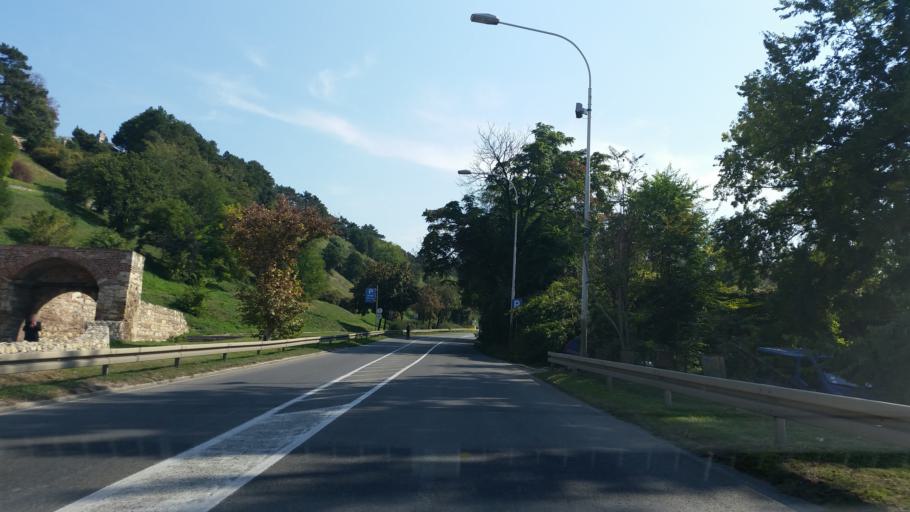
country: RS
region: Central Serbia
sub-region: Belgrade
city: Stari Grad
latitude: 44.8217
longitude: 20.4475
